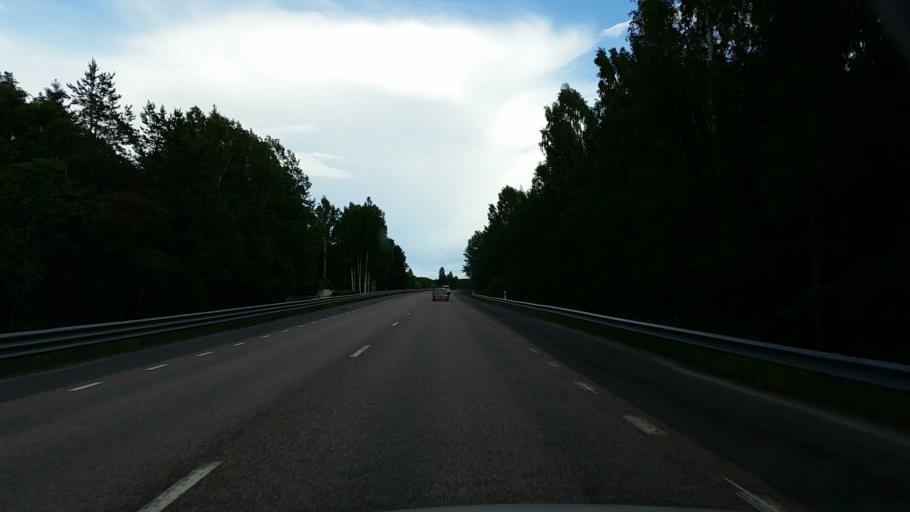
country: SE
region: Vaestmanland
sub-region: Fagersta Kommun
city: Fagersta
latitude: 59.9761
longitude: 15.7025
